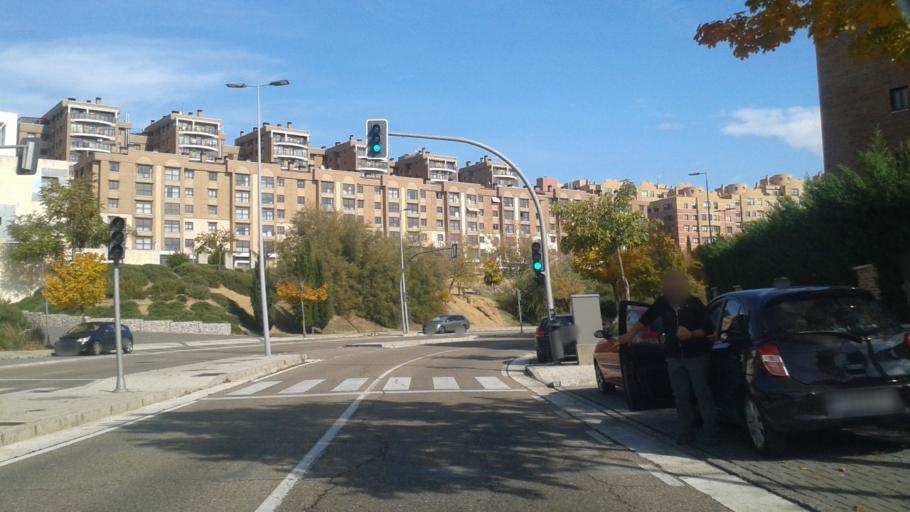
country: ES
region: Castille and Leon
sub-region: Provincia de Valladolid
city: Zaratan
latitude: 41.6341
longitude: -4.7651
